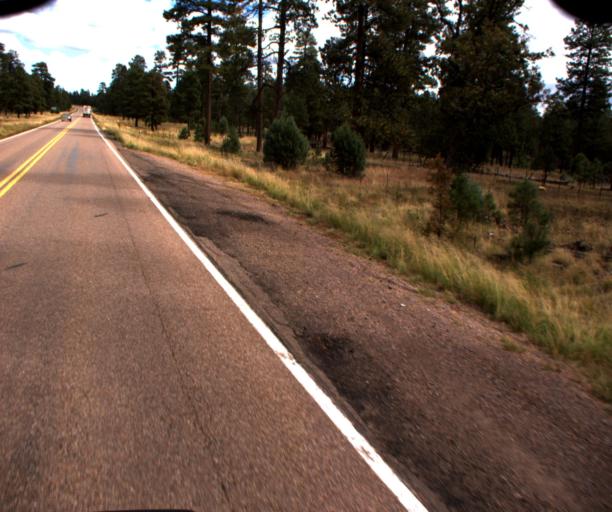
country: US
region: Arizona
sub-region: Navajo County
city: Heber-Overgaard
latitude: 34.3705
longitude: -110.6836
